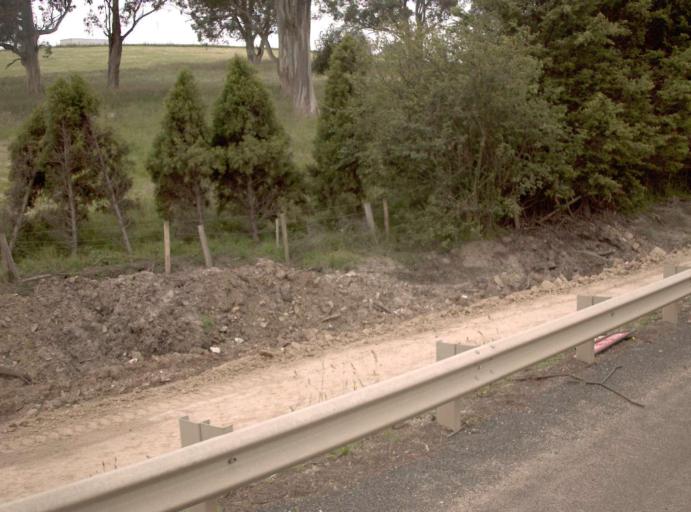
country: AU
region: Victoria
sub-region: Latrobe
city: Moe
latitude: -38.3973
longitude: 146.1146
